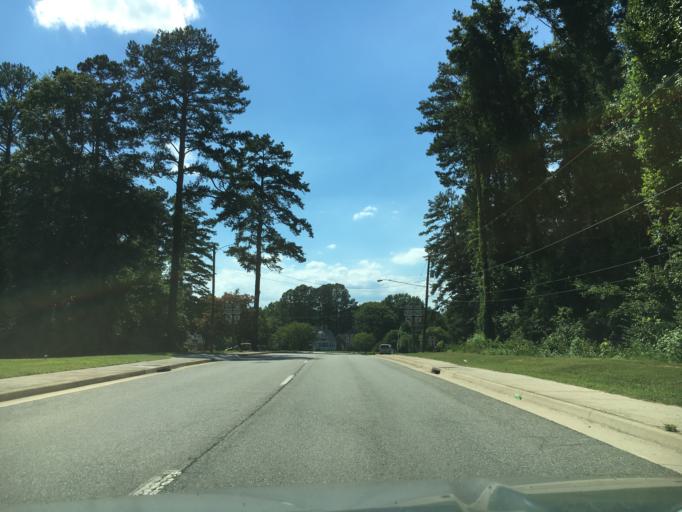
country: US
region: Virginia
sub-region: Halifax County
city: South Boston
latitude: 36.7079
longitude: -78.9093
